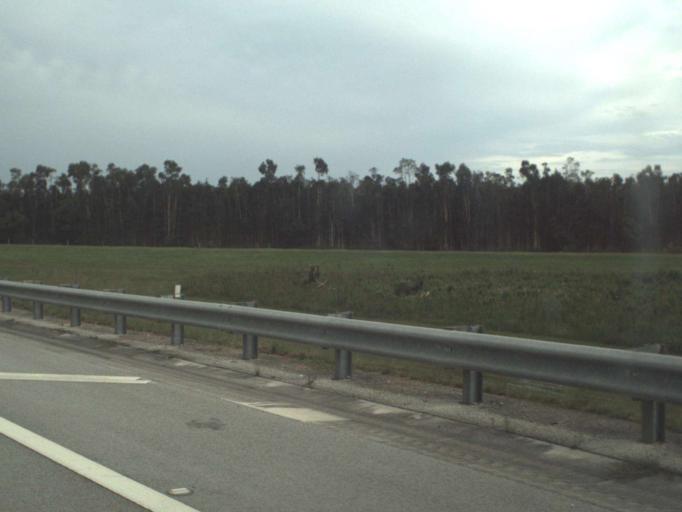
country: US
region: Florida
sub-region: Miami-Dade County
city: Palm Springs North
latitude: 25.9422
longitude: -80.3491
